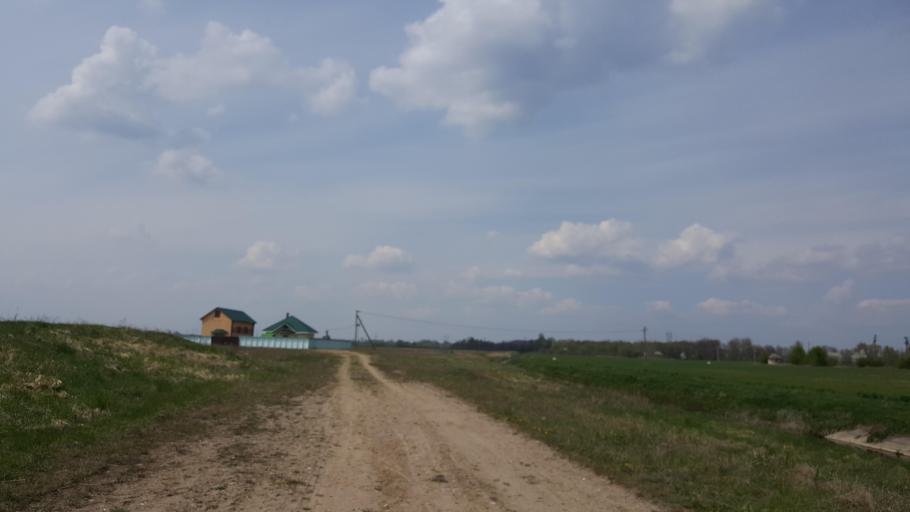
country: BY
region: Brest
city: Zhabinka
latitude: 52.2019
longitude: 23.9879
